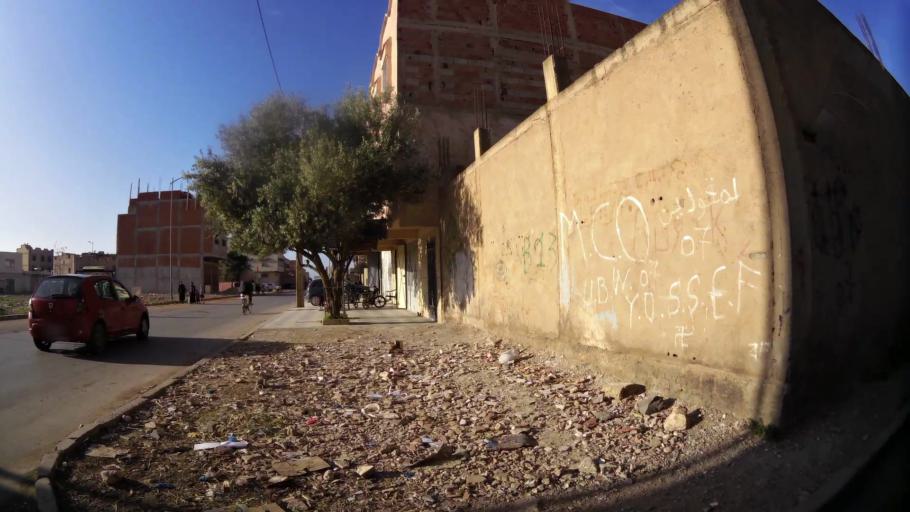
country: MA
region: Oriental
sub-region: Oujda-Angad
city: Oujda
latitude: 34.7087
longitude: -1.8966
